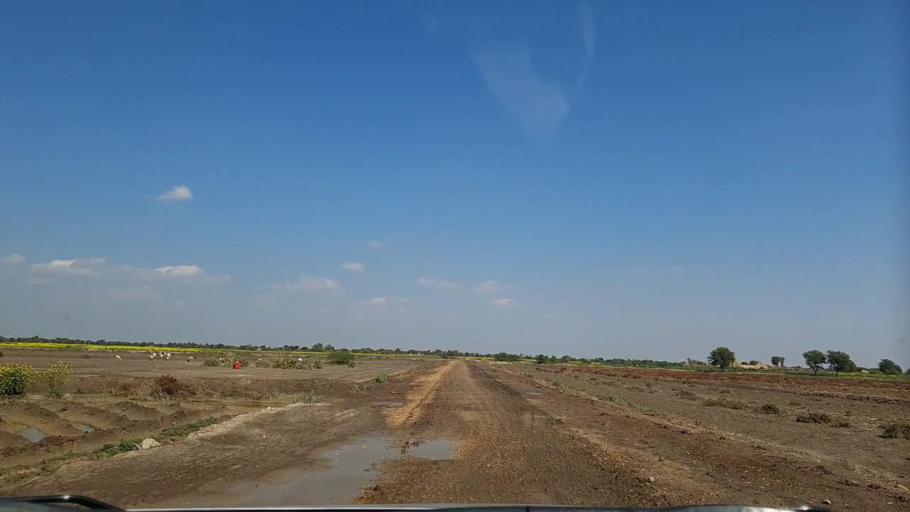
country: PK
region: Sindh
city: Pithoro
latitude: 25.6881
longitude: 69.3697
